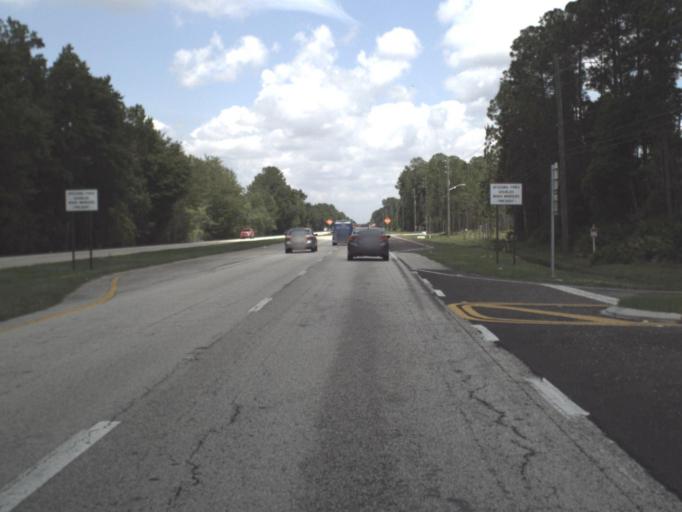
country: US
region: Florida
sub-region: Saint Johns County
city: Palm Valley
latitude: 30.1169
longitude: -81.4912
